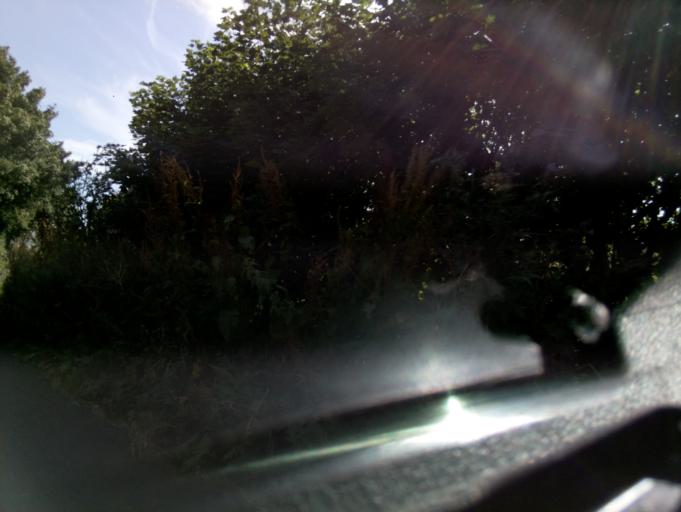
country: GB
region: England
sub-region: Gloucestershire
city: Tetbury
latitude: 51.6652
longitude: -2.1447
